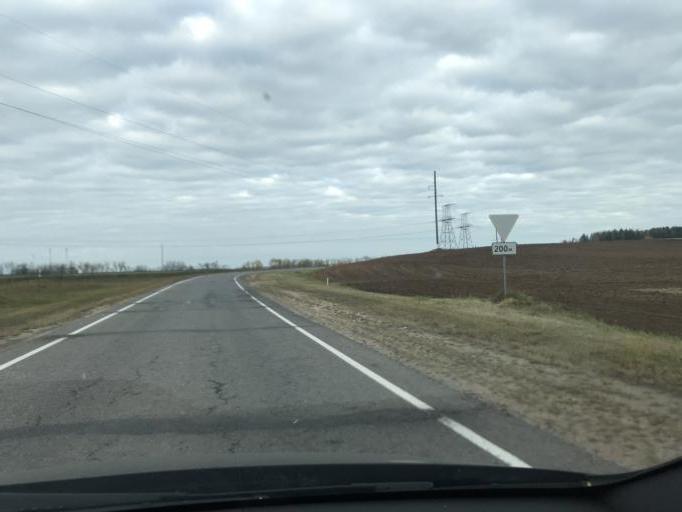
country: BY
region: Minsk
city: Astrashytski Haradok
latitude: 54.0551
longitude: 27.7074
